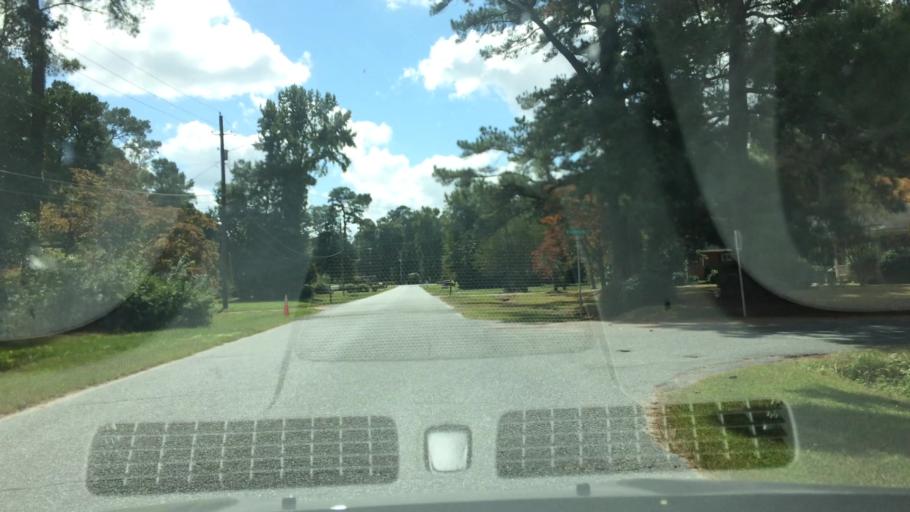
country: US
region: North Carolina
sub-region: Pitt County
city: Ayden
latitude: 35.4745
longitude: -77.4368
